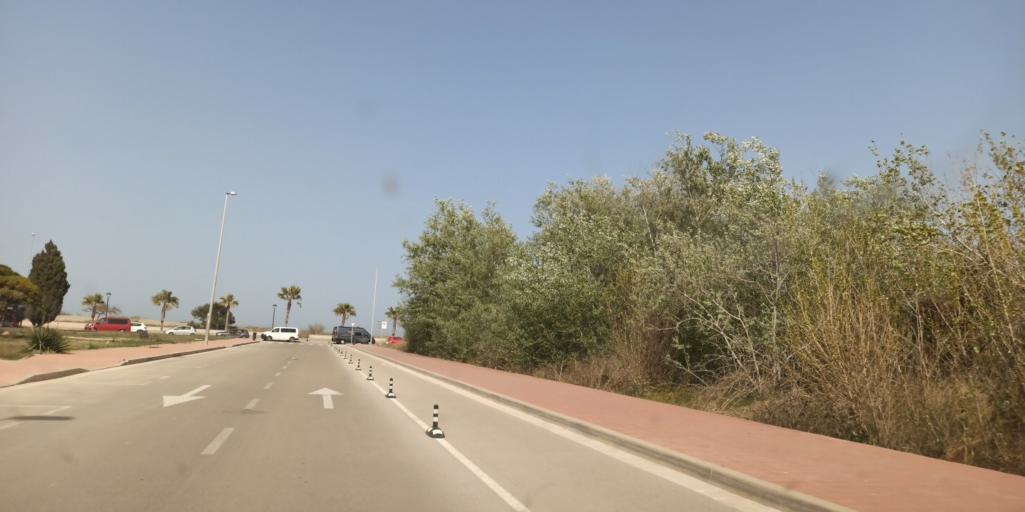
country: ES
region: Catalonia
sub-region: Provincia de Tarragona
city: Deltebre
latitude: 40.7258
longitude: 0.8436
